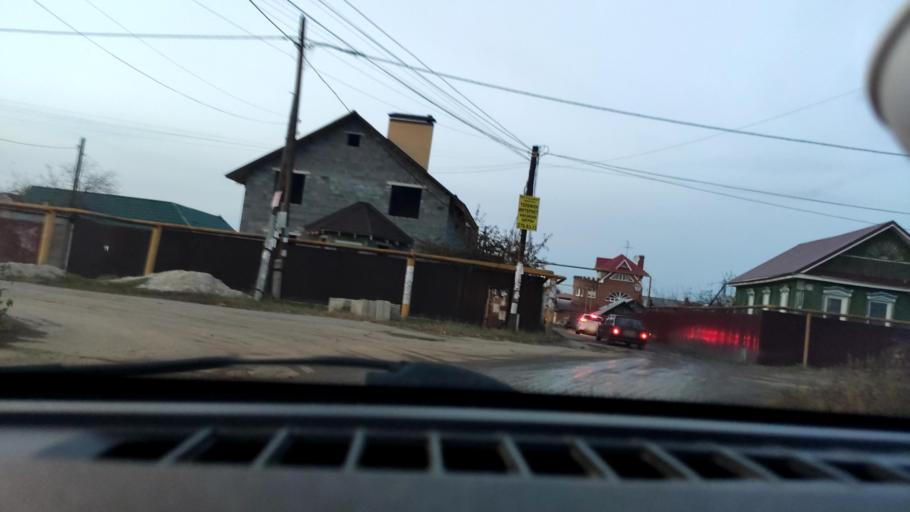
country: RU
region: Samara
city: Samara
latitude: 53.1351
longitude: 50.0950
